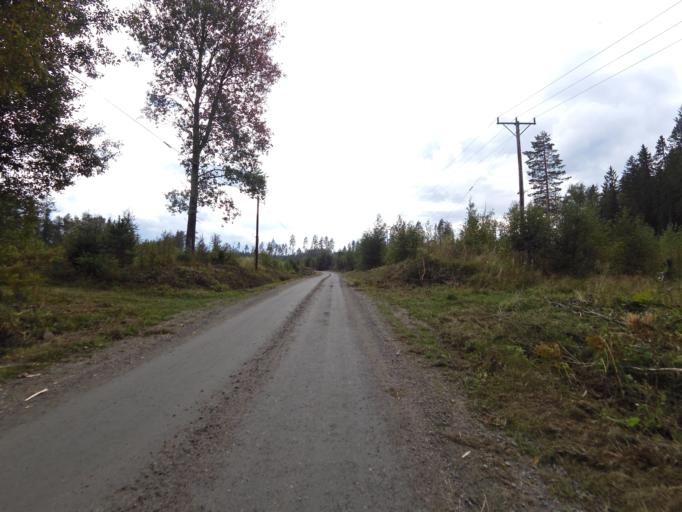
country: SE
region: Gaevleborg
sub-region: Sandvikens Kommun
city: Sandviken
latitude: 60.7214
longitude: 16.8139
